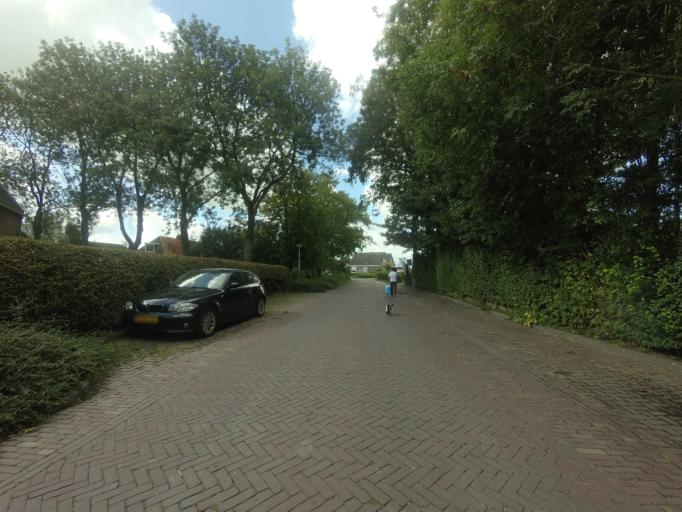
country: NL
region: Friesland
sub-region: Sudwest Fryslan
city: Sneek
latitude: 53.0591
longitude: 5.6265
